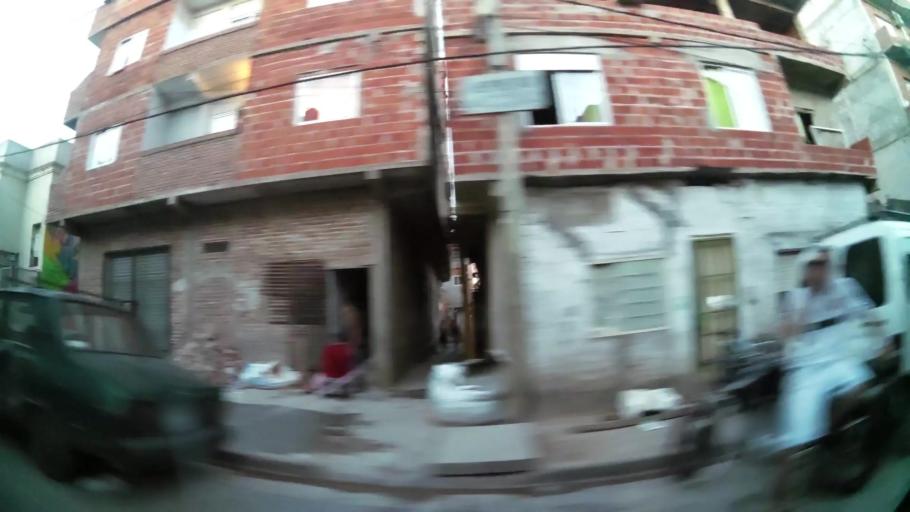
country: AR
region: Buenos Aires F.D.
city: Villa Lugano
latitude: -34.6779
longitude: -58.4679
